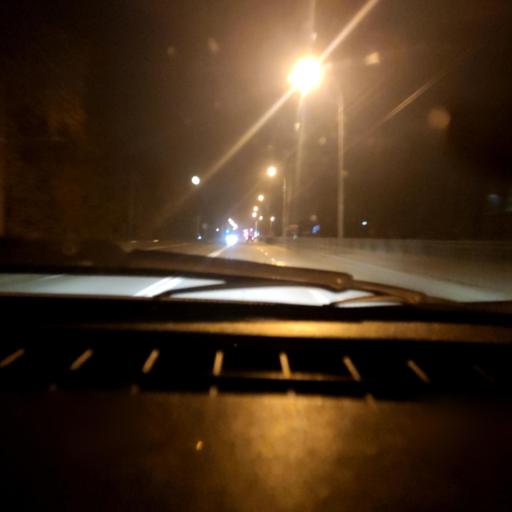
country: RU
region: Bashkortostan
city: Ufa
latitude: 54.7980
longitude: 56.1220
